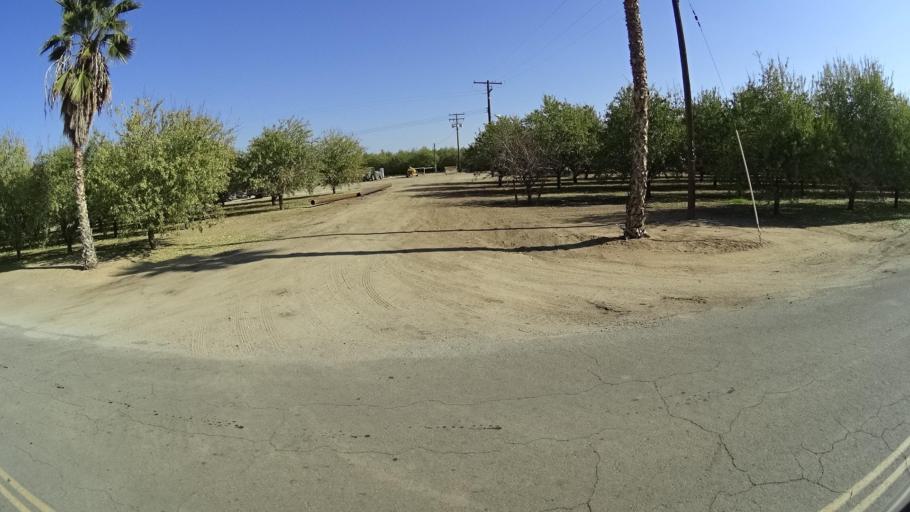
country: US
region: California
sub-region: Tulare County
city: Richgrove
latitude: 35.7169
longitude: -119.1339
